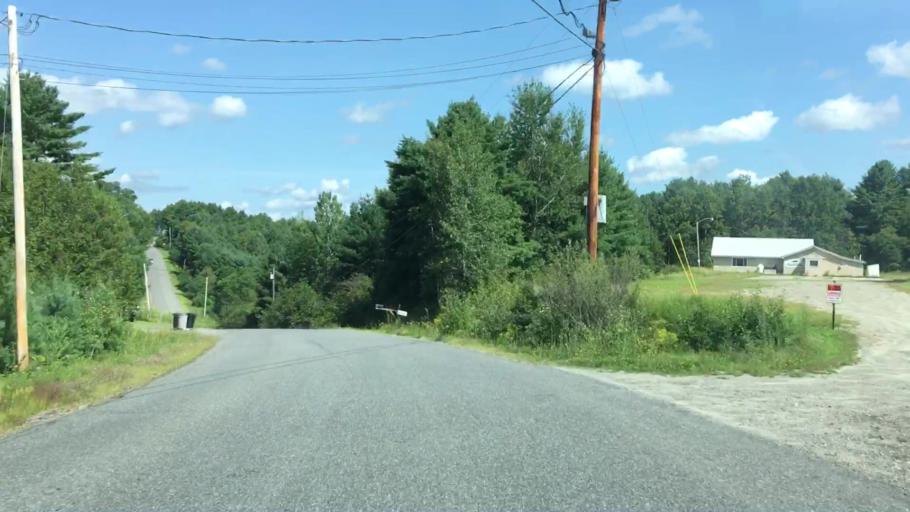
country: US
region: Maine
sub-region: Kennebec County
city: Manchester
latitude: 44.3629
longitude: -69.8152
